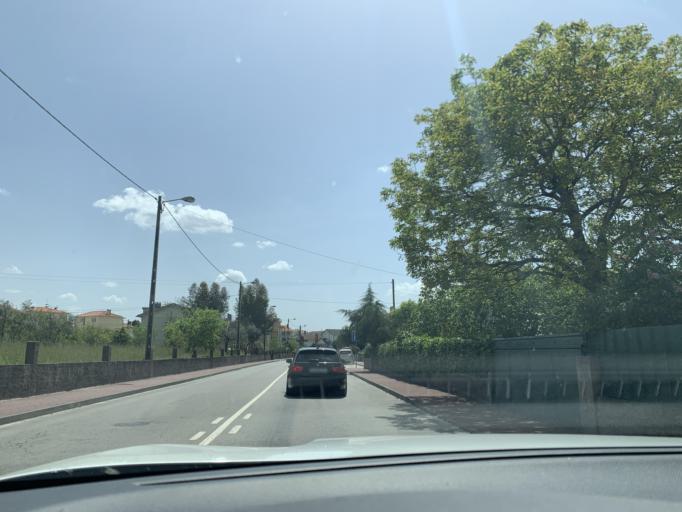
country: PT
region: Viseu
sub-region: Mangualde
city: Mangualde
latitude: 40.6075
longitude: -7.7476
